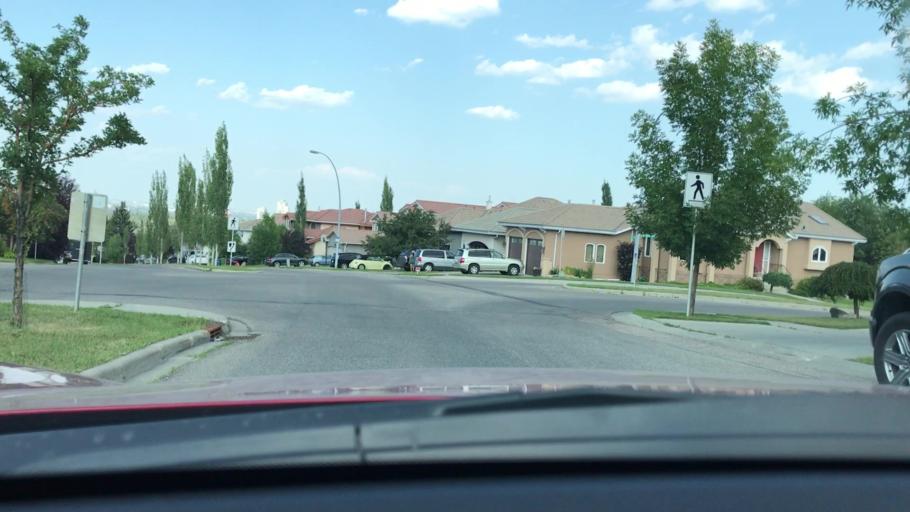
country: CA
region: Alberta
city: Calgary
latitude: 51.0306
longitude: -114.1752
